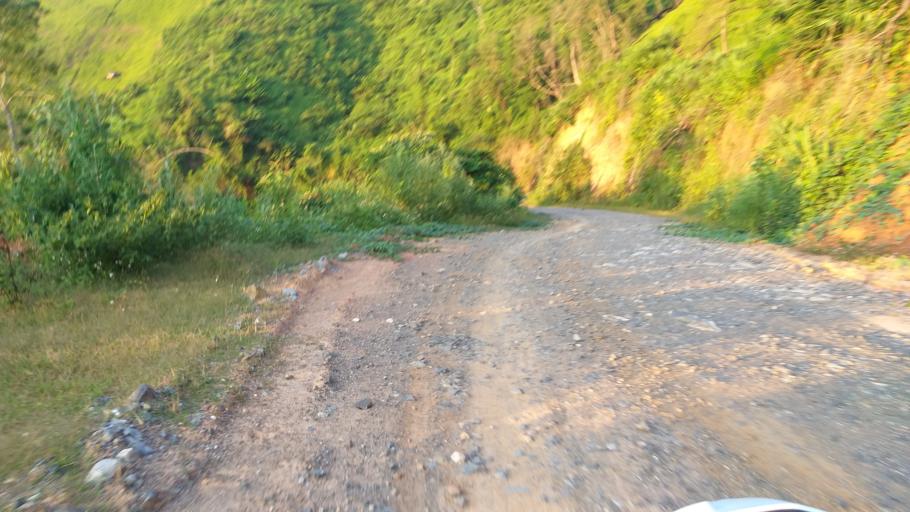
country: LA
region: Phongsali
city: Khoa
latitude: 21.1875
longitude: 102.5428
